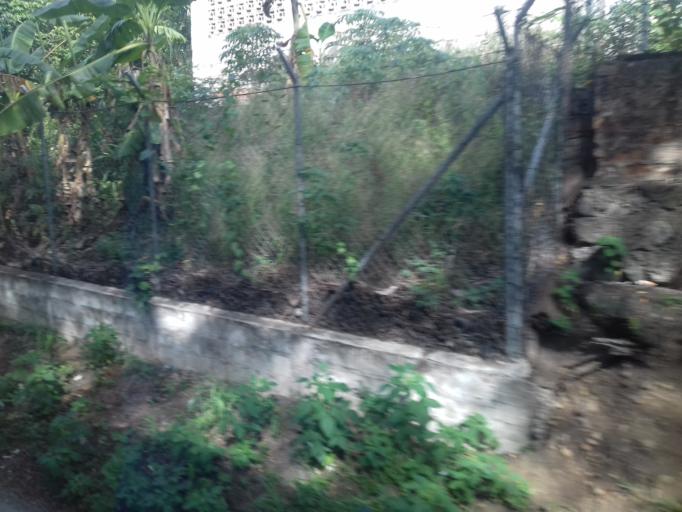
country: CO
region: Antioquia
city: Venecia
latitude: 5.9697
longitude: -75.8370
